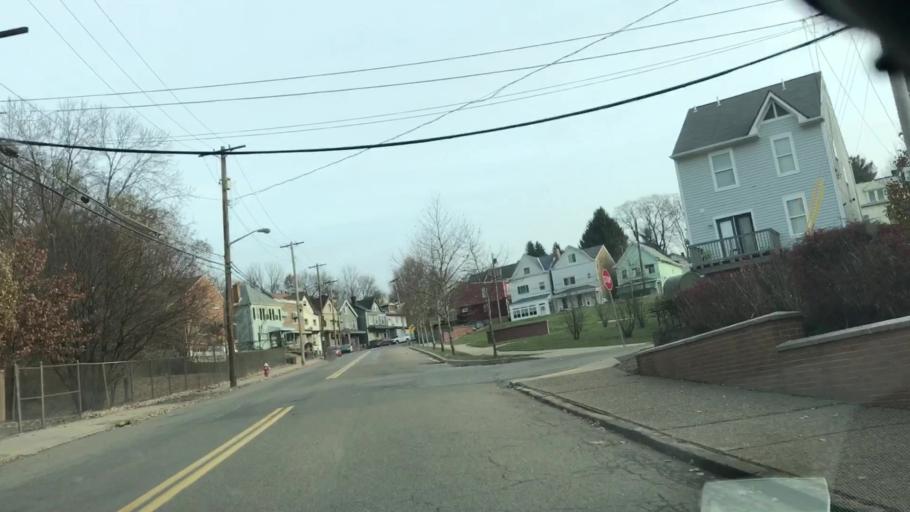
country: US
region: Pennsylvania
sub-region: Allegheny County
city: Bellevue
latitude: 40.4668
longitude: -80.0320
